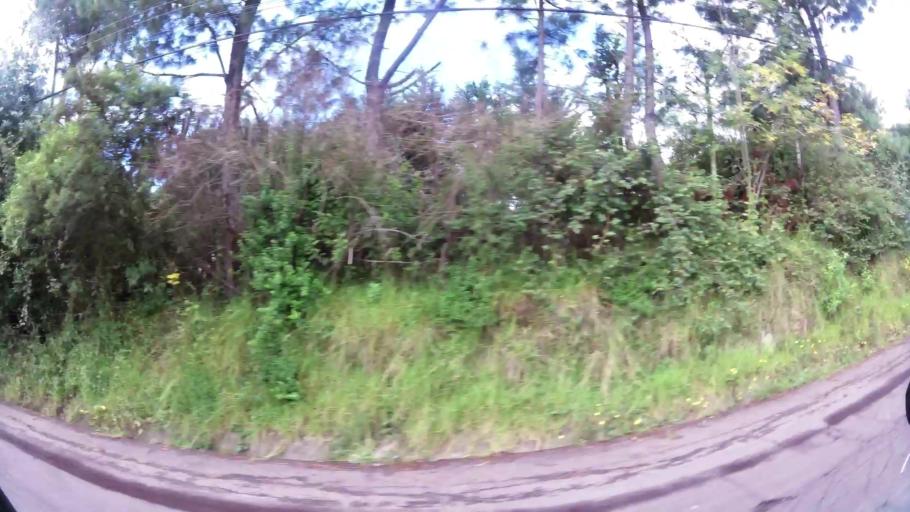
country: EC
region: Pichincha
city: Sangolqui
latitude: -0.3194
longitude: -78.3987
